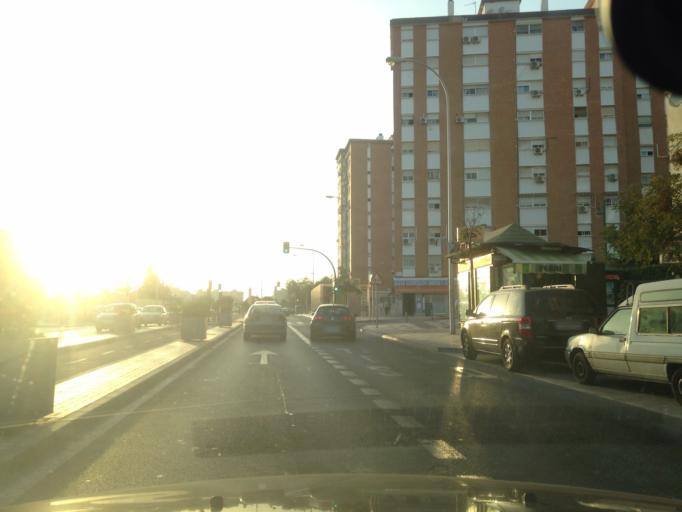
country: ES
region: Andalusia
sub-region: Provincia de Malaga
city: Malaga
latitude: 36.7193
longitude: -4.4523
